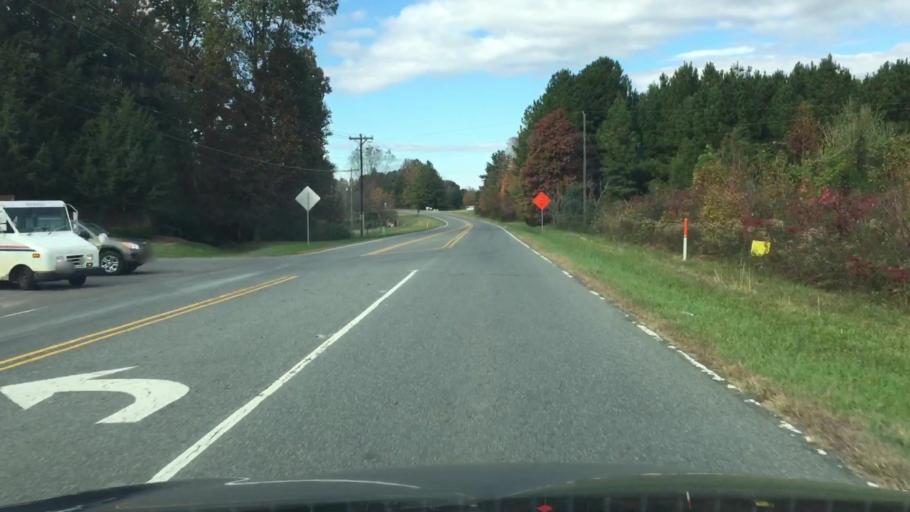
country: US
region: North Carolina
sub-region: Iredell County
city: Troutman
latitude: 35.6524
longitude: -80.8446
